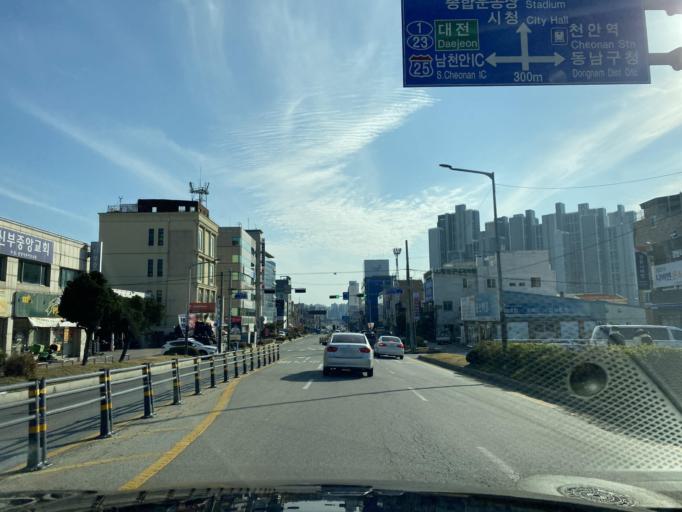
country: KR
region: Chungcheongnam-do
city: Cheonan
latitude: 36.8096
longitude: 127.1585
